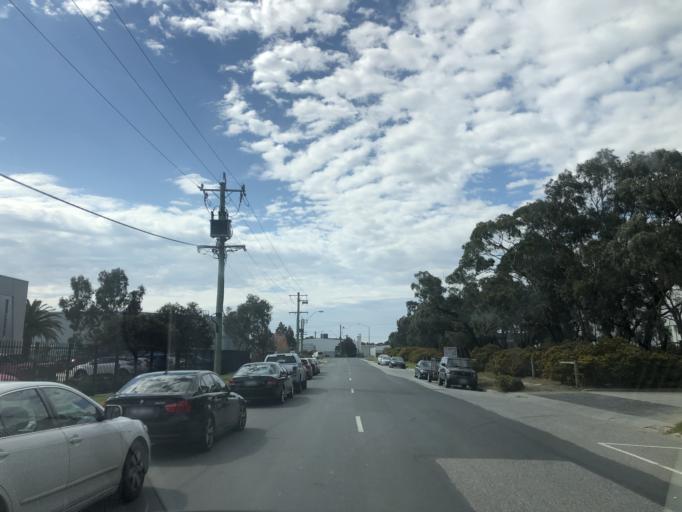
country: AU
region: Victoria
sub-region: Casey
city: Hampton Park
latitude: -38.0356
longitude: 145.2286
